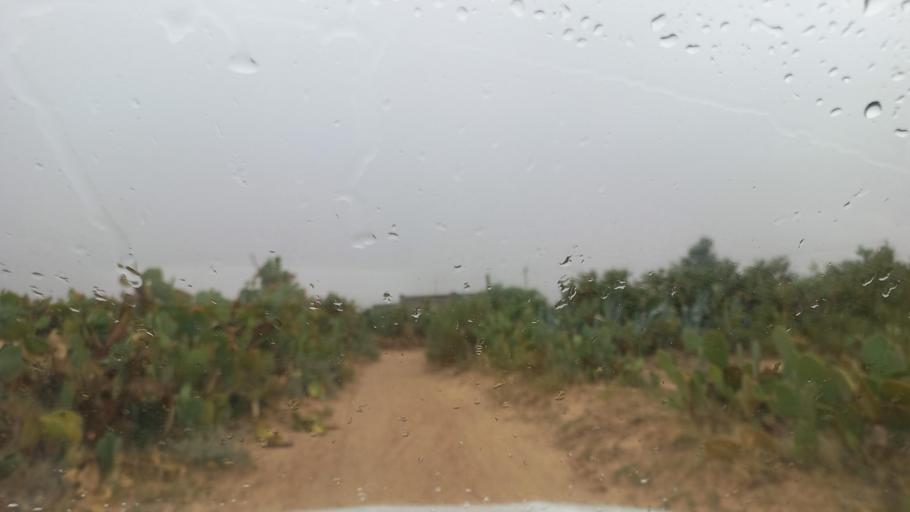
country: TN
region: Al Qasrayn
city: Kasserine
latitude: 35.2718
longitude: 8.9443
